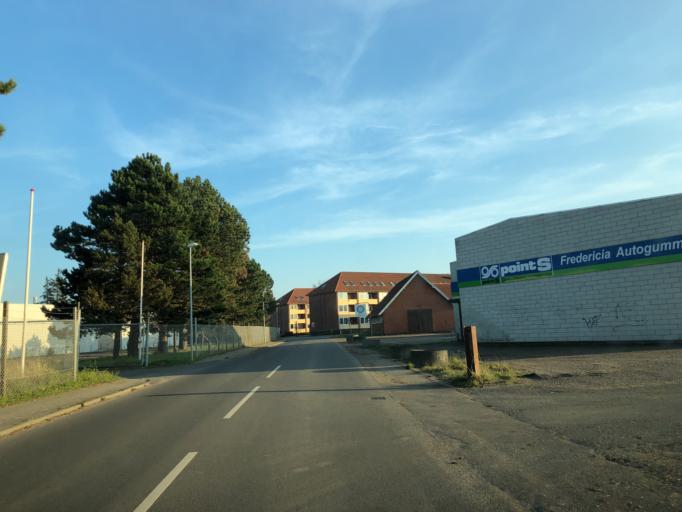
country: DK
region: South Denmark
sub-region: Fredericia Kommune
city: Fredericia
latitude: 55.5779
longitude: 9.7423
